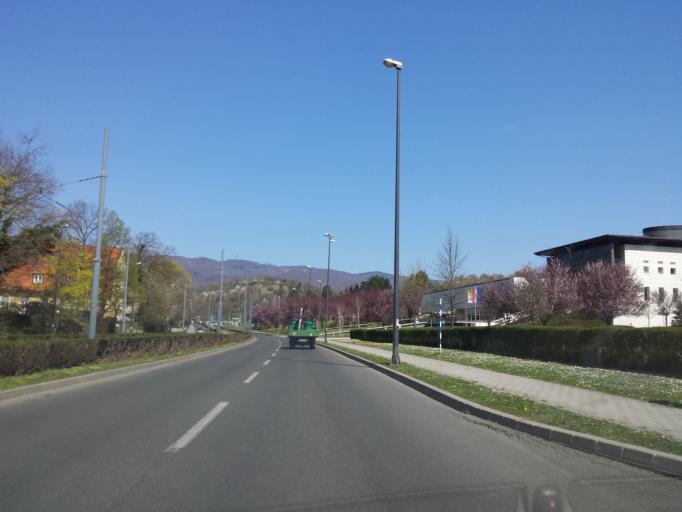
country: HR
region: Grad Zagreb
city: Zagreb
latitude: 45.8370
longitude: 15.9775
